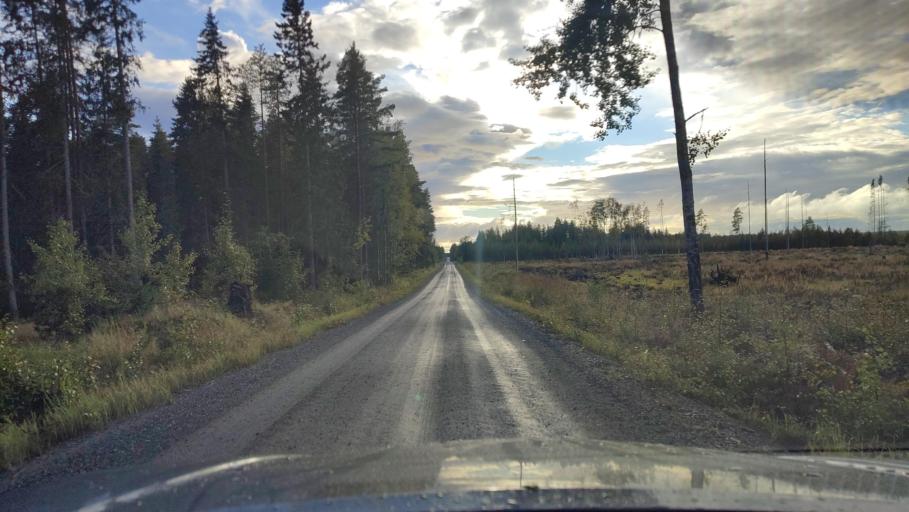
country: FI
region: Ostrobothnia
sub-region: Sydosterbotten
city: Kristinestad
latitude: 62.3025
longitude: 21.5134
